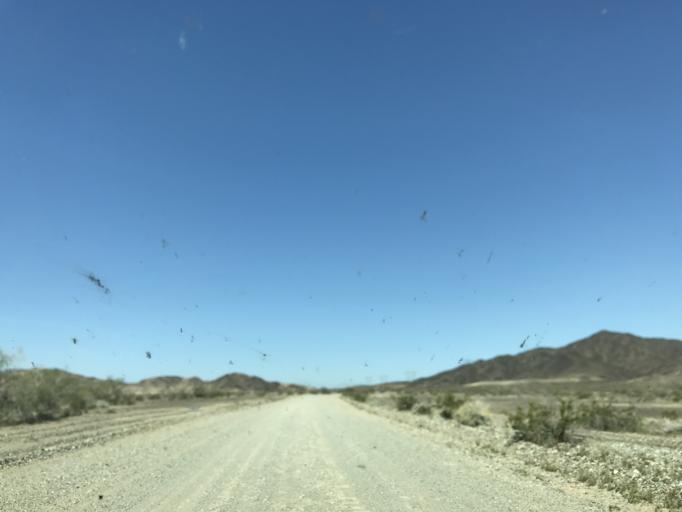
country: US
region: California
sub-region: Riverside County
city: Mesa Verde
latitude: 33.4936
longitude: -114.8175
